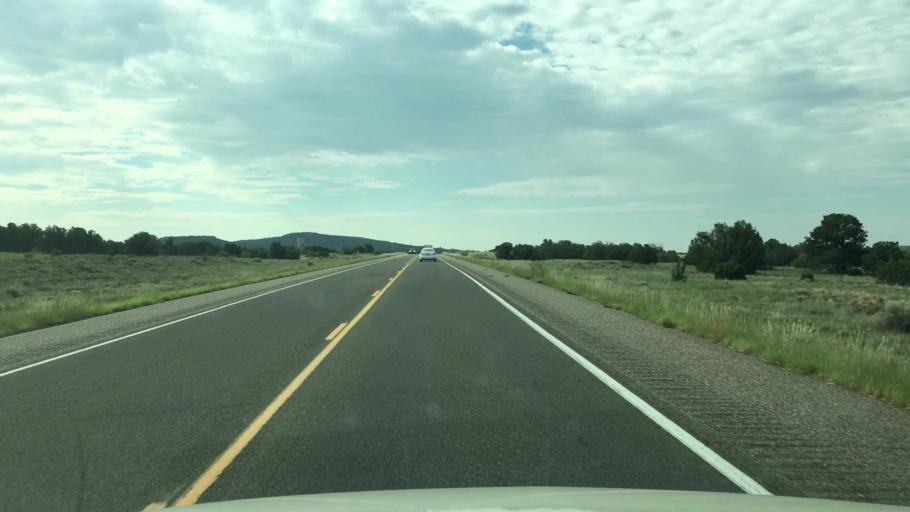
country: US
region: New Mexico
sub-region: Santa Fe County
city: Eldorado at Santa Fe
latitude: 35.3333
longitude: -105.8361
